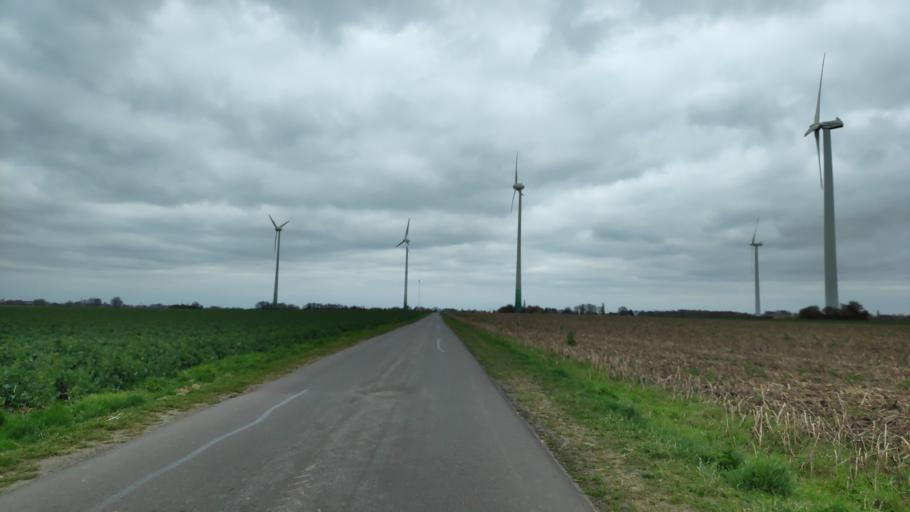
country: DE
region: North Rhine-Westphalia
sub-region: Regierungsbezirk Detmold
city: Minden
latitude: 52.3132
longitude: 8.8432
